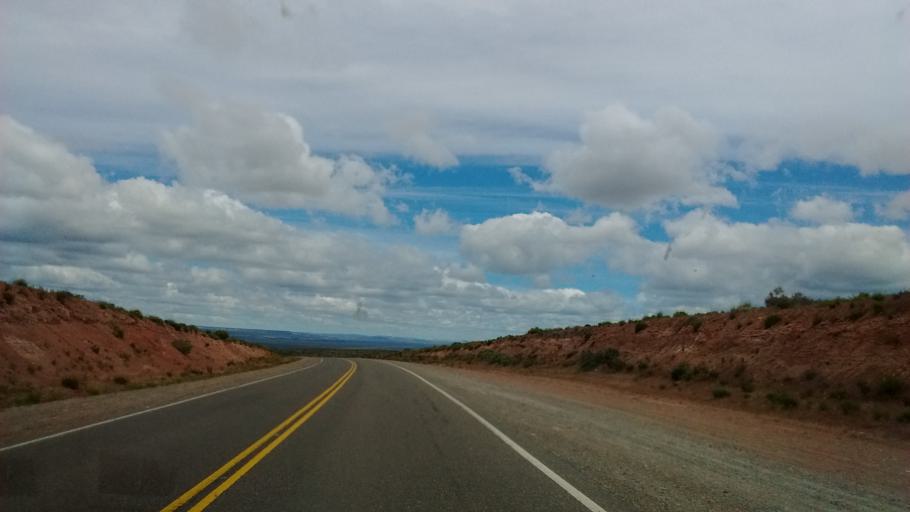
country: AR
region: Neuquen
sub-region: Departamento de Picun Leufu
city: Picun Leufu
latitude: -39.7570
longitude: -69.6435
